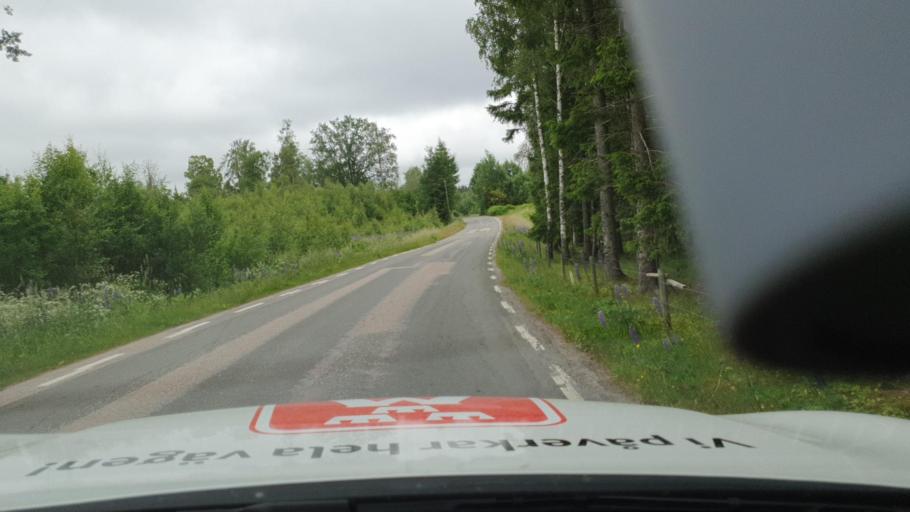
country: SE
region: Vaestra Goetaland
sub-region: Tibro Kommun
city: Tibro
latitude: 58.3565
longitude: 14.1985
